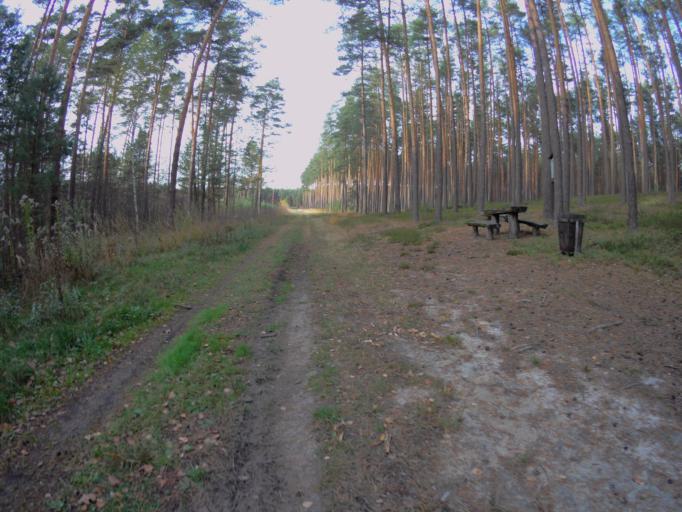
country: PL
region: Subcarpathian Voivodeship
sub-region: Powiat kolbuszowski
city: Lipnica
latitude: 50.3303
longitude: 21.9328
